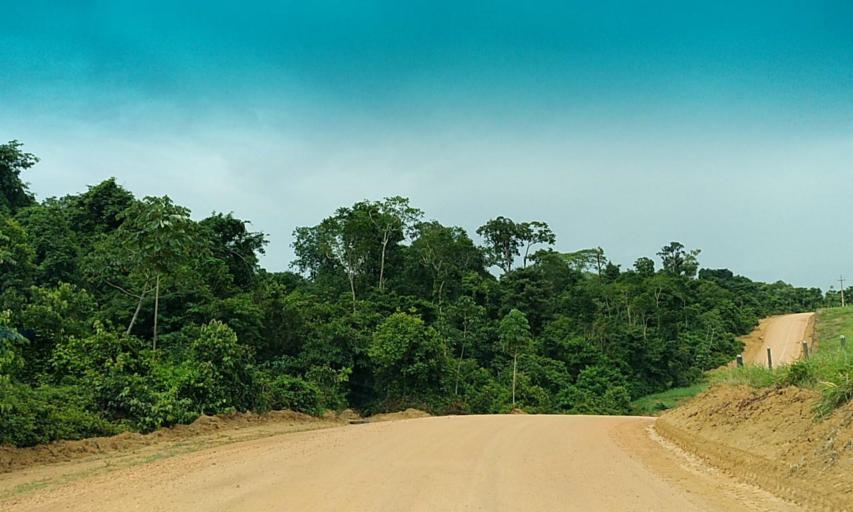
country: BR
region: Para
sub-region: Senador Jose Porfirio
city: Senador Jose Porfirio
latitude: -3.0585
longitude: -51.6734
